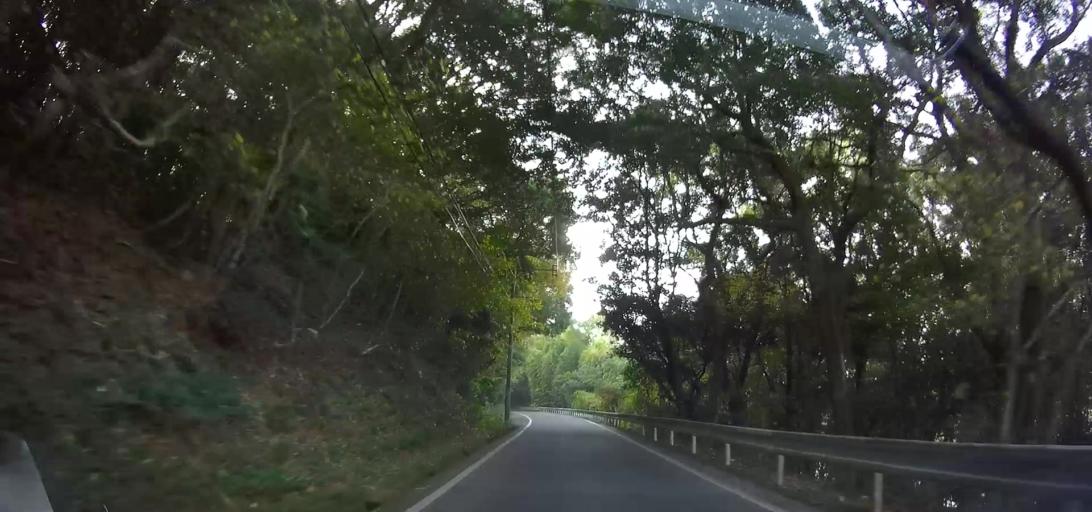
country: JP
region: Nagasaki
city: Shimabara
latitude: 32.6845
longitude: 130.2003
